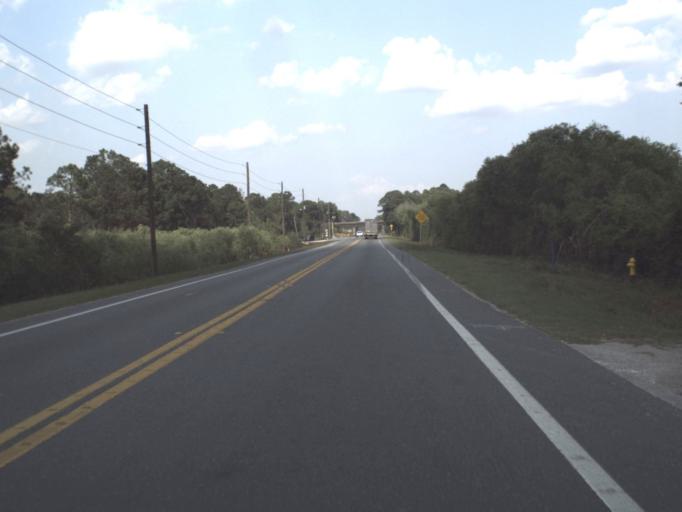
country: US
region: Florida
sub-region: Lake County
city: Howie In The Hills
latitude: 28.6450
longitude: -81.8036
